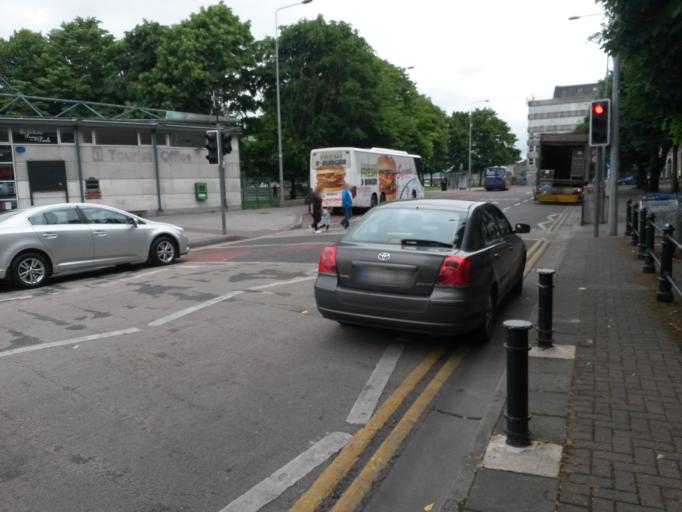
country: IE
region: Munster
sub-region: County Limerick
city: Luimneach
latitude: 52.6648
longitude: -8.6263
